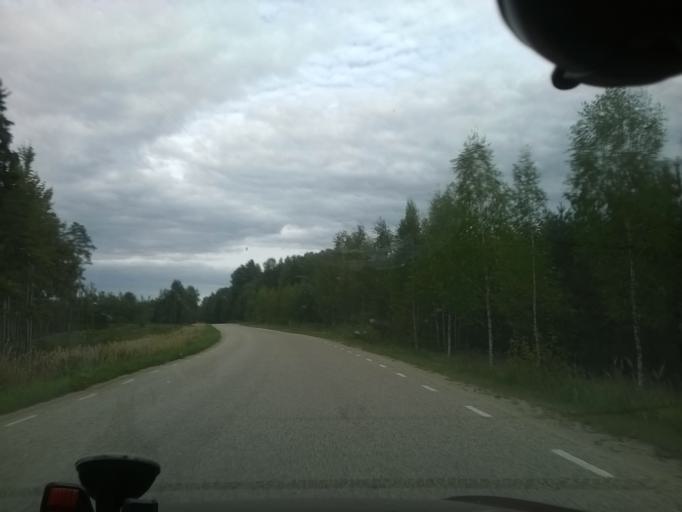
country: EE
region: Vorumaa
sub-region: Voru linn
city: Voru
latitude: 57.7599
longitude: 26.9993
